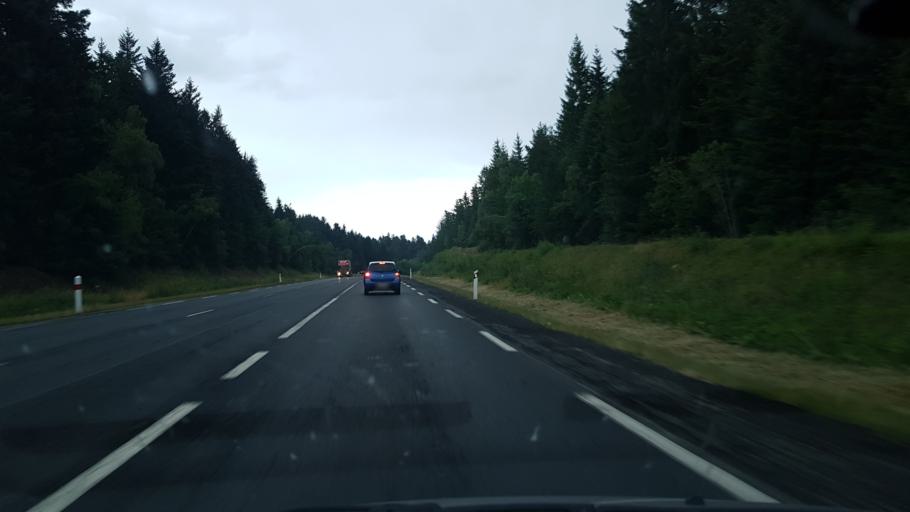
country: FR
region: Auvergne
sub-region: Departement de la Haute-Loire
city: Allegre
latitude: 45.1484
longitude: 3.6481
